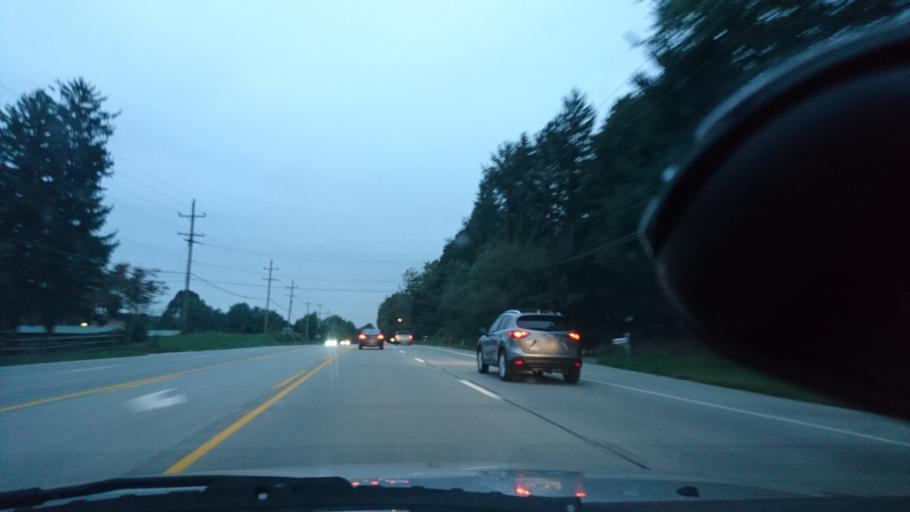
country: US
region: Pennsylvania
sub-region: Delaware County
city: Brookhaven
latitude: 39.8830
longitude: -75.4001
